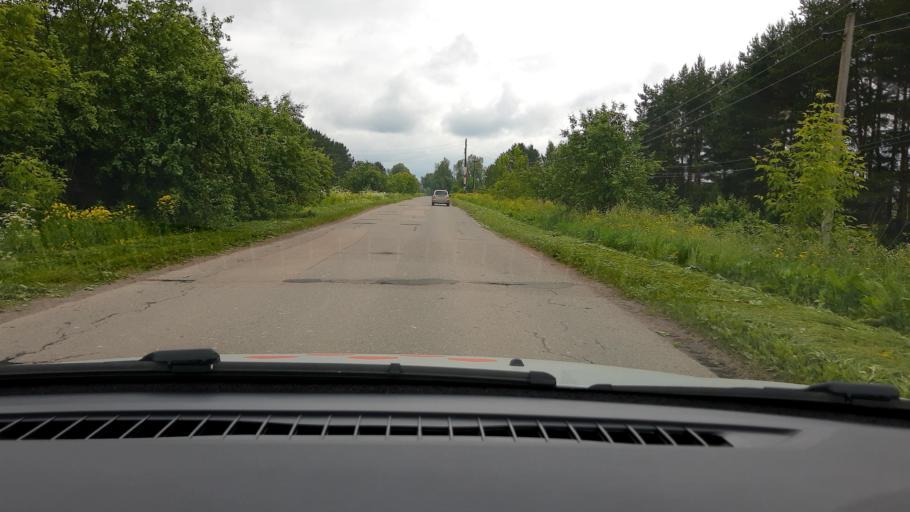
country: RU
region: Nizjnij Novgorod
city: Bogorodsk
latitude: 56.0804
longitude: 43.5114
